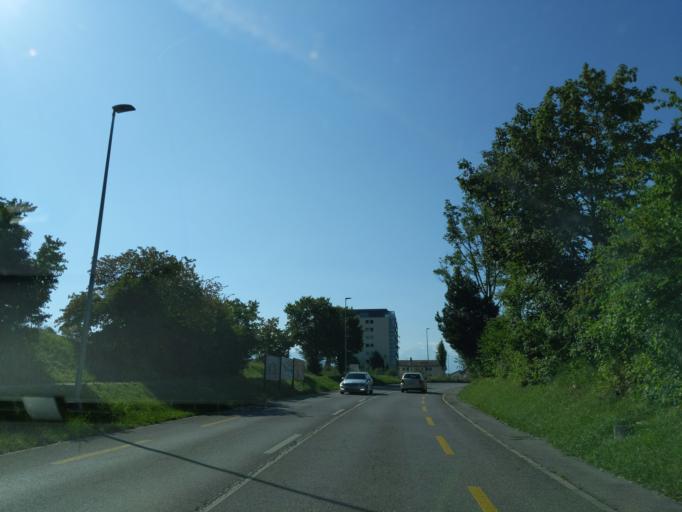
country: CH
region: Bern
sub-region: Thun District
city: Thun
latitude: 46.7561
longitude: 7.6097
